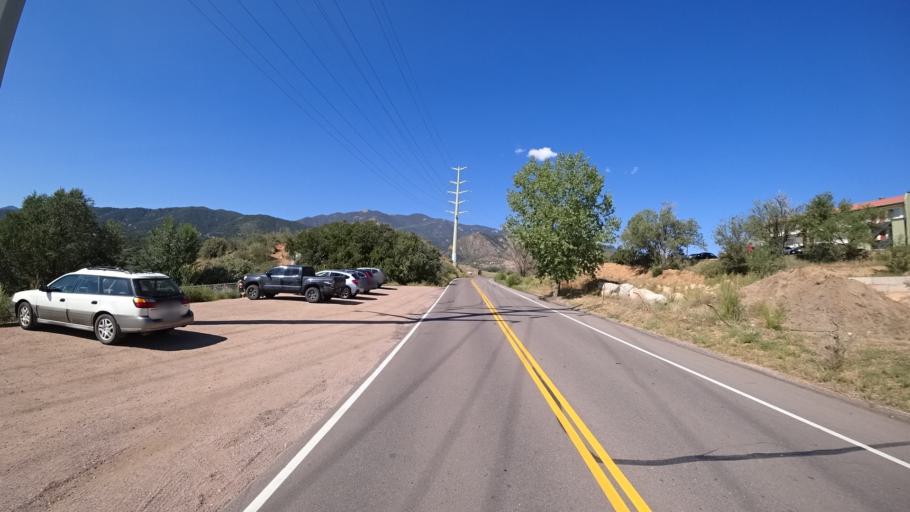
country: US
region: Colorado
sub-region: El Paso County
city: Colorado Springs
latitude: 38.8282
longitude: -104.8627
